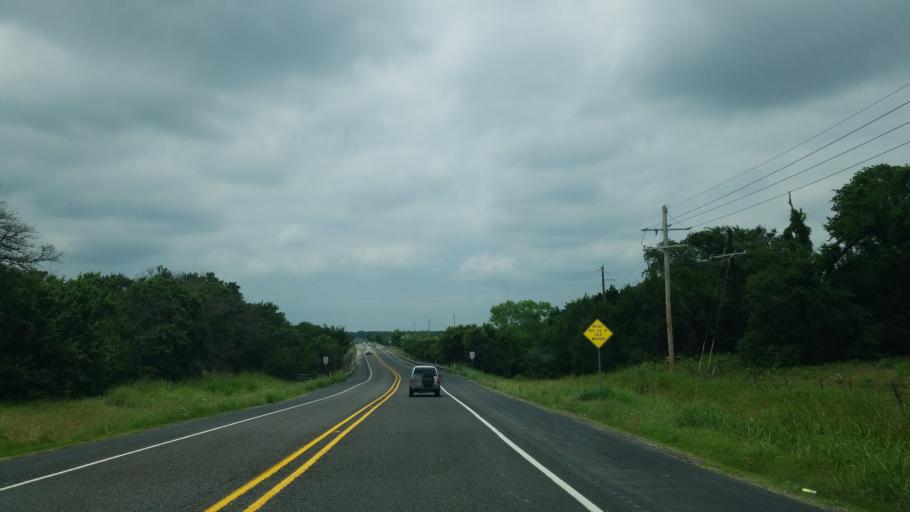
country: US
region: Texas
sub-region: Denton County
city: Pilot Point
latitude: 33.4429
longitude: -96.9254
